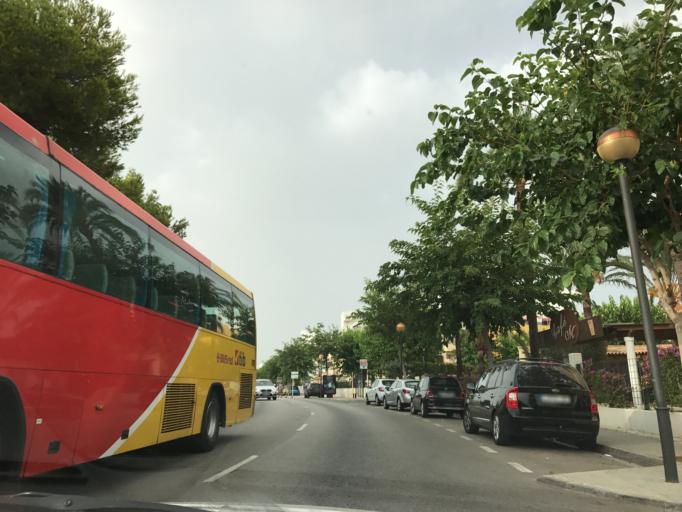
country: ES
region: Balearic Islands
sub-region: Illes Balears
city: Son Servera
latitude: 39.5975
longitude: 3.3810
